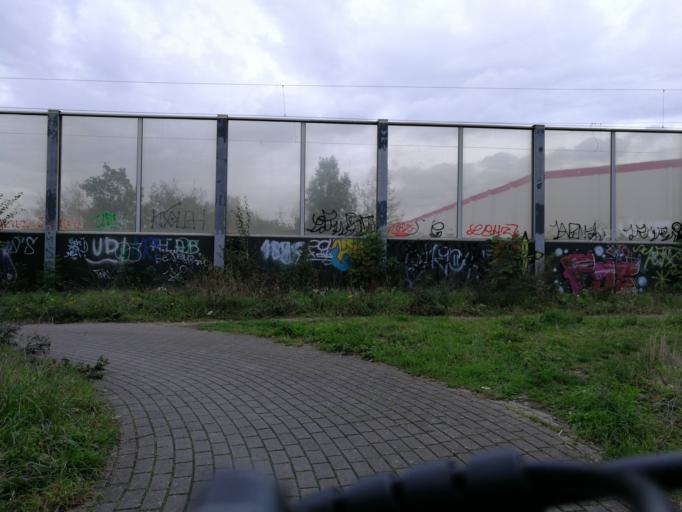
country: DE
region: North Rhine-Westphalia
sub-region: Regierungsbezirk Dusseldorf
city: Dusseldorf
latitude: 51.1454
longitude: 6.7523
